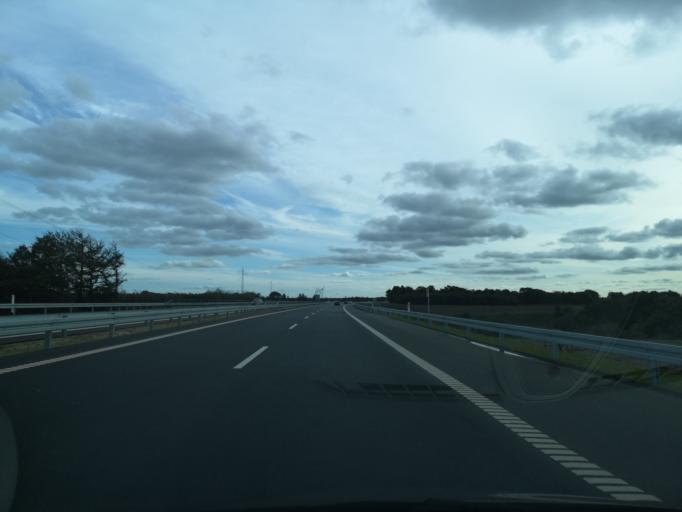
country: DK
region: Central Jutland
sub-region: Herning Kommune
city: Avlum
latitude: 56.3596
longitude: 8.7315
